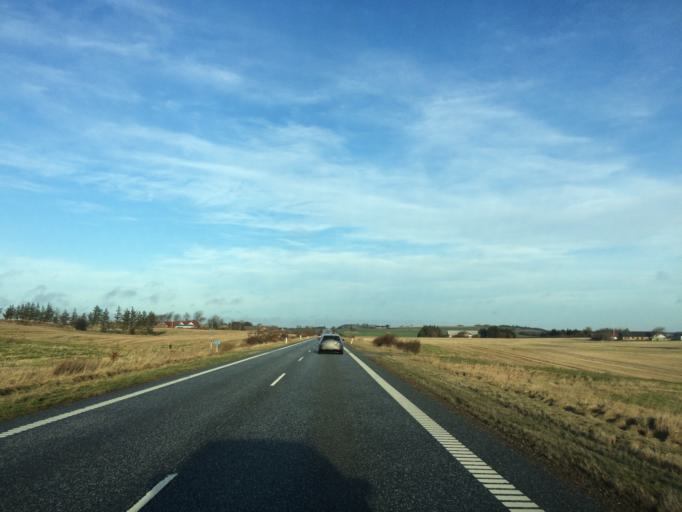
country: DK
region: North Denmark
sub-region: Thisted Kommune
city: Hurup
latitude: 56.8042
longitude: 8.4768
